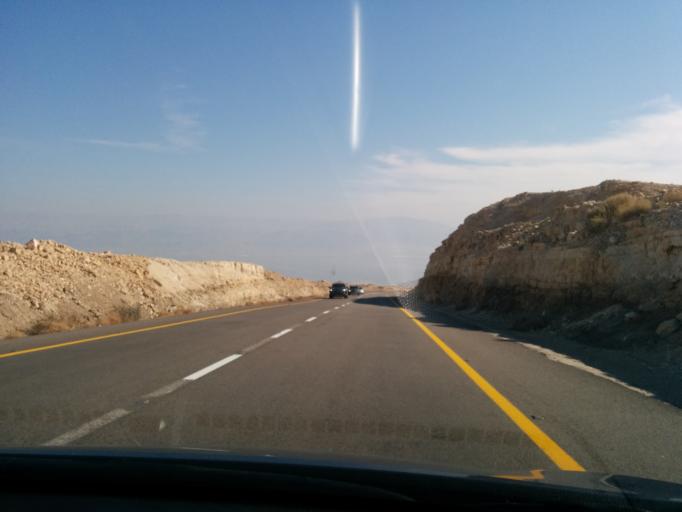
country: IL
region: Southern District
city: `En Boqeq
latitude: 31.1589
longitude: 35.3319
